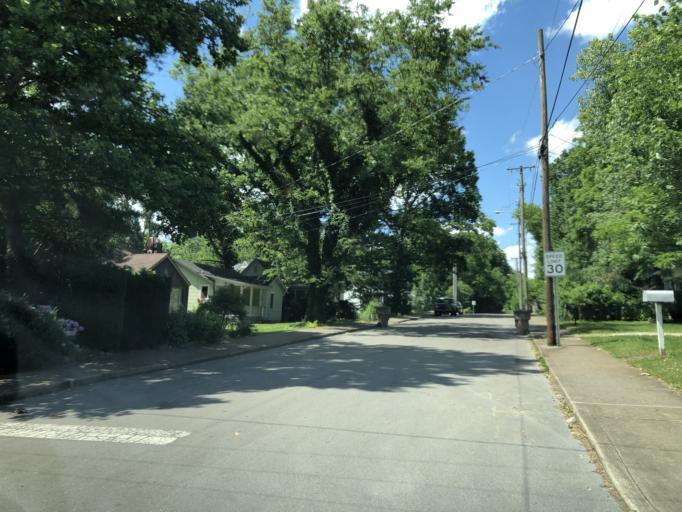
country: US
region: Tennessee
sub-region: Davidson County
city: Nashville
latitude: 36.1863
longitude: -86.7356
